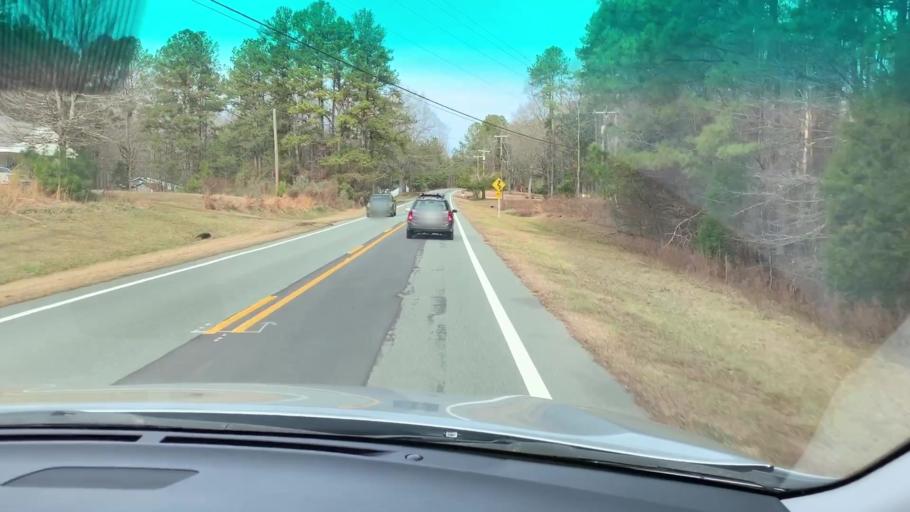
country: US
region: North Carolina
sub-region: Wake County
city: Green Level
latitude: 35.8576
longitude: -78.9405
